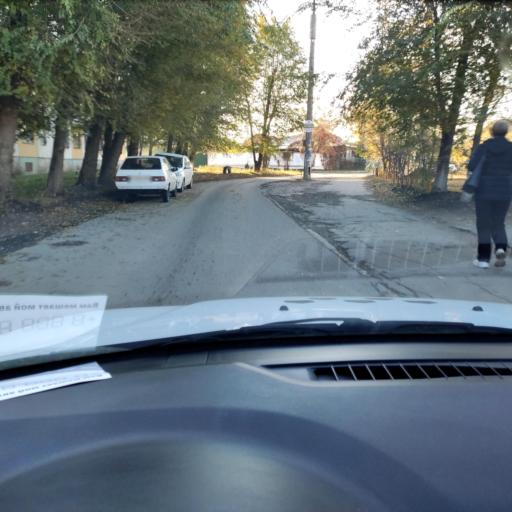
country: RU
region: Samara
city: Tol'yatti
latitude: 53.5318
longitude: 49.4257
